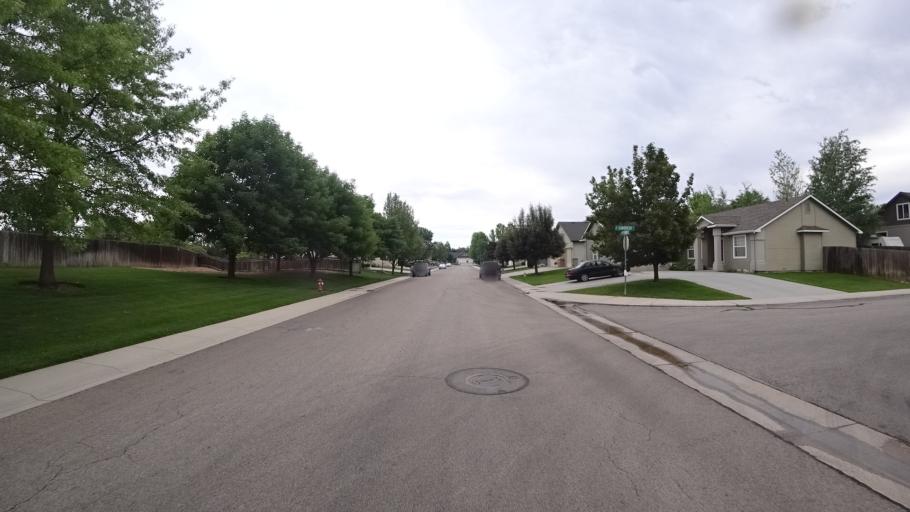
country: US
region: Idaho
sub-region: Ada County
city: Meridian
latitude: 43.5848
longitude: -116.3273
